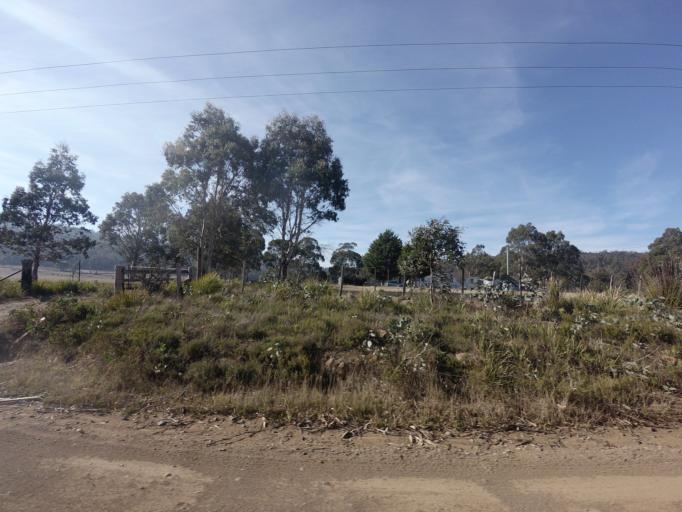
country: AU
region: Tasmania
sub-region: Sorell
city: Sorell
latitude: -42.4916
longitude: 147.5237
